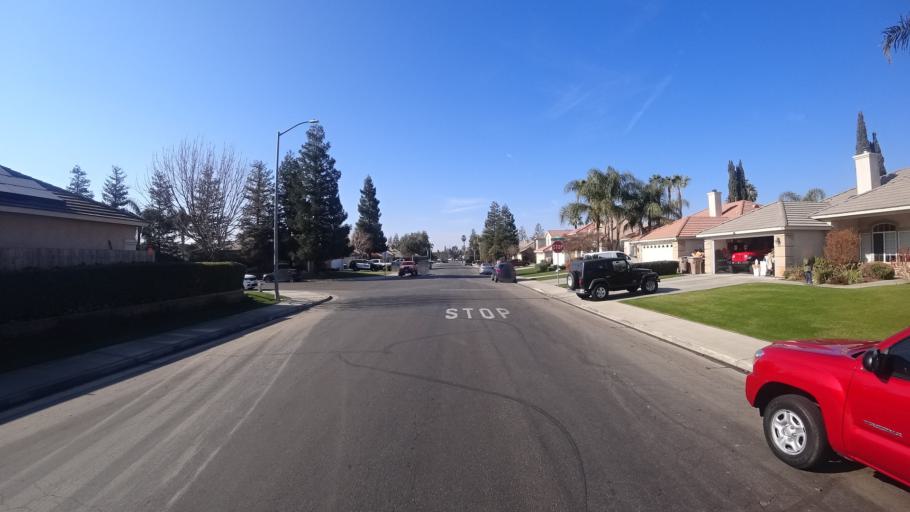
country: US
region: California
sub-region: Kern County
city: Greenacres
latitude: 35.3189
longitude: -119.1209
